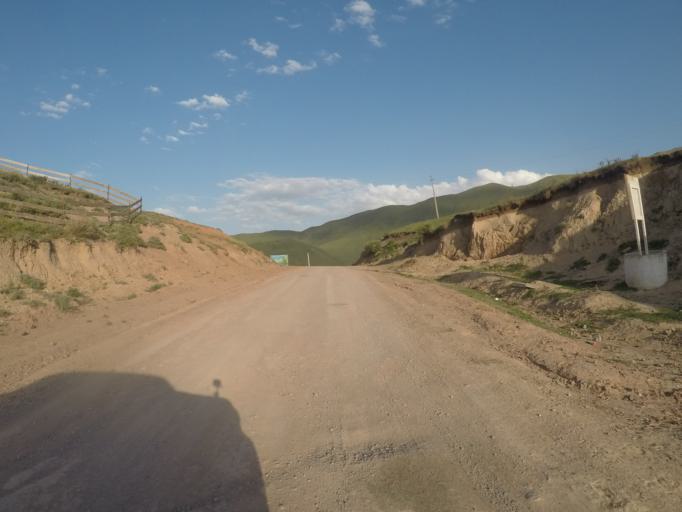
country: KG
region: Chuy
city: Bishkek
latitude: 42.6428
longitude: 74.6289
